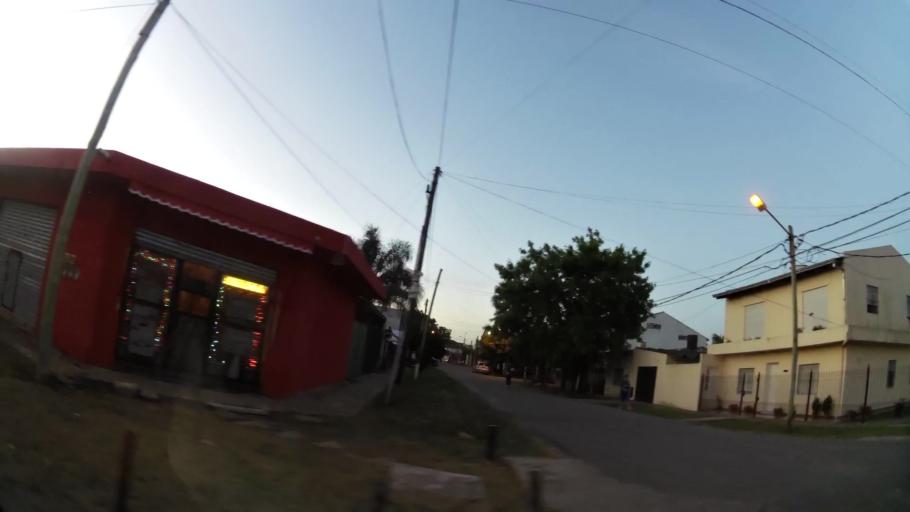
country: AR
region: Buenos Aires
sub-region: Partido de Quilmes
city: Quilmes
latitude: -34.7798
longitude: -58.2230
